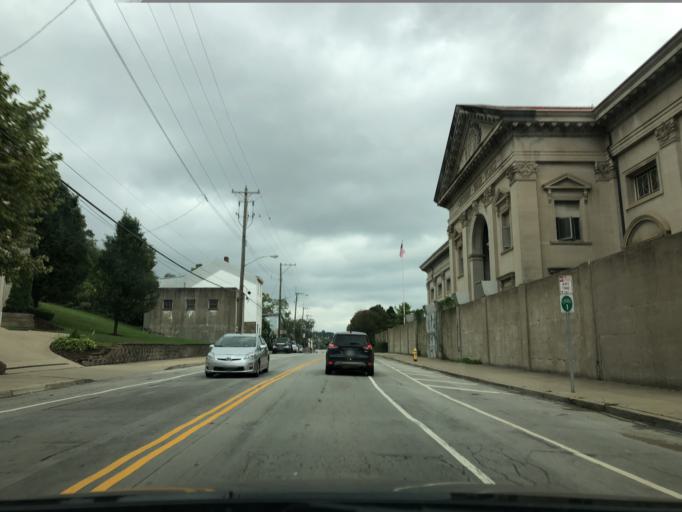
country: US
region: Kentucky
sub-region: Campbell County
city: Dayton
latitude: 39.1239
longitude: -84.4609
